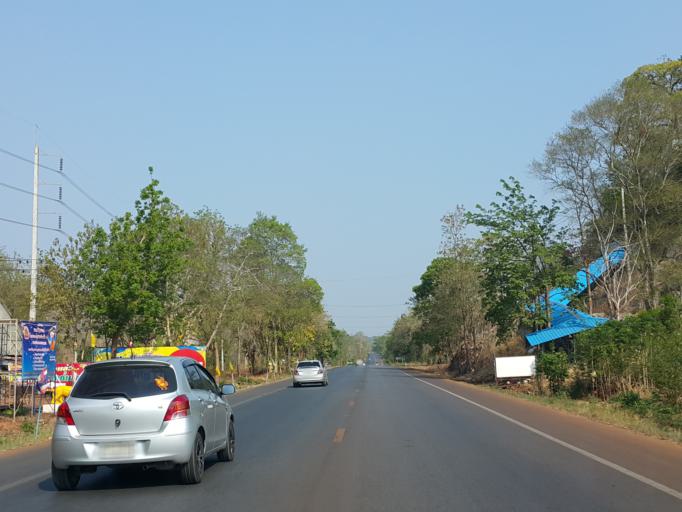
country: TH
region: Kanchanaburi
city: Sai Yok
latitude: 14.1019
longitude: 99.2277
